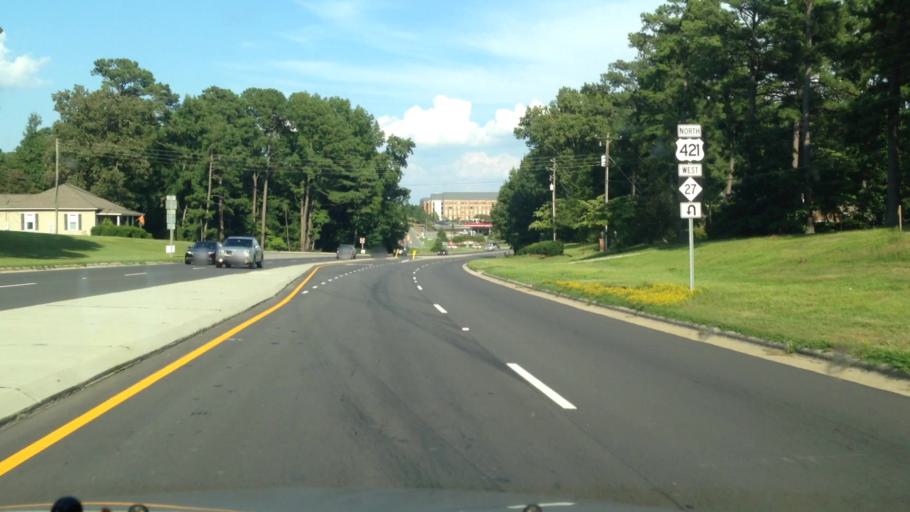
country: US
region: North Carolina
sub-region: Harnett County
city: Buies Creek
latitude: 35.4075
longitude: -78.7508
